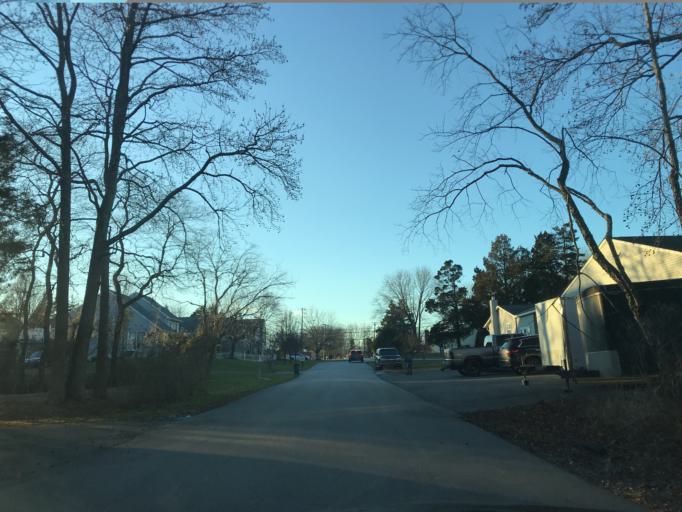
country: US
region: Maryland
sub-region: Baltimore County
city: Bowleys Quarters
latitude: 39.3708
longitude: -76.3507
